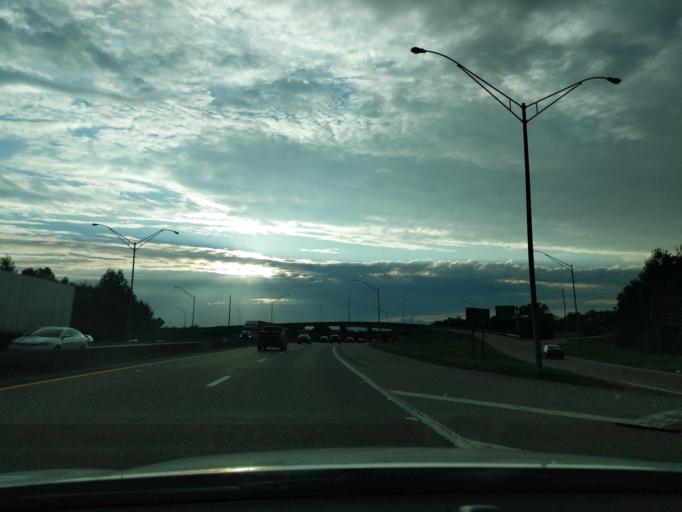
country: US
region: Tennessee
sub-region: Shelby County
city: New South Memphis
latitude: 35.0784
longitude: -90.0538
